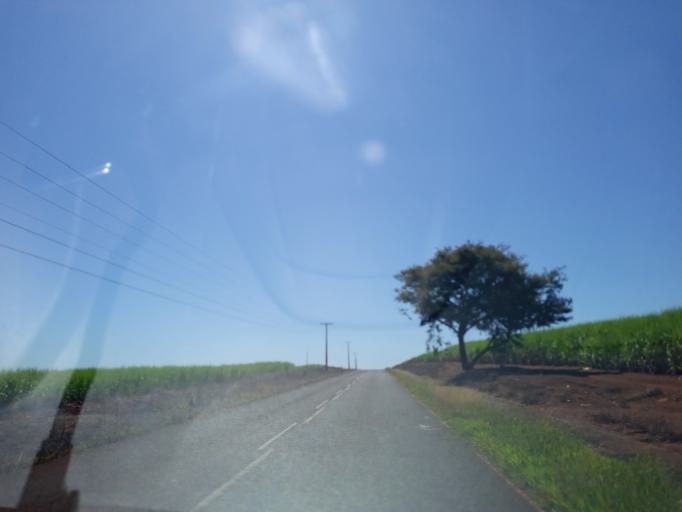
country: BR
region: Goias
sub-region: Itumbiara
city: Itumbiara
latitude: -18.4249
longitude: -49.1684
